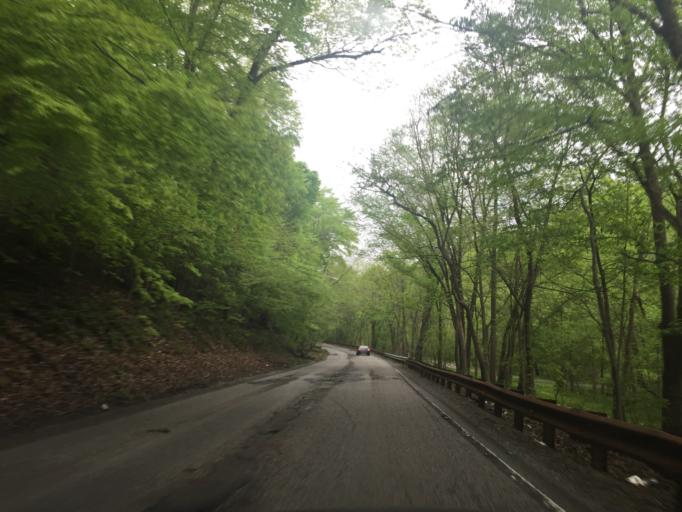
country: US
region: Maryland
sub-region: Baltimore County
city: Charlestown
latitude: 39.3044
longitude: -76.6895
